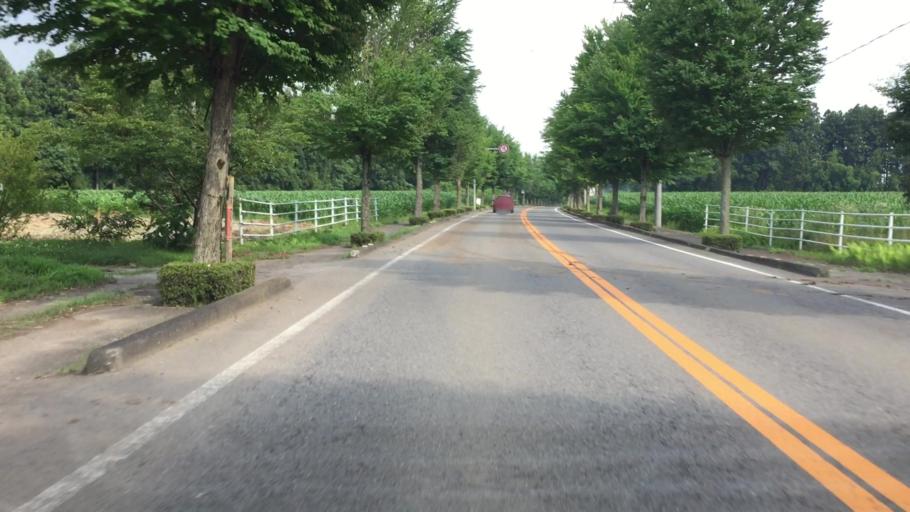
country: JP
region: Tochigi
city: Kuroiso
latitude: 36.9853
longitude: 139.9575
